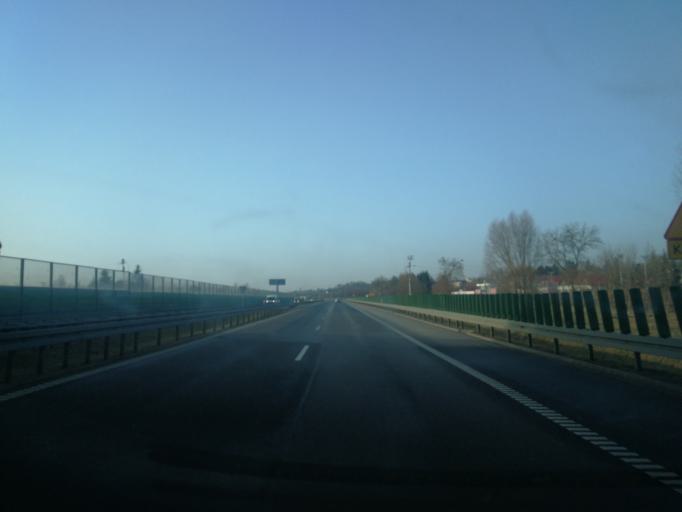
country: PL
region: Warmian-Masurian Voivodeship
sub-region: Powiat elblaski
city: Gronowo Gorne
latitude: 54.1321
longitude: 19.4571
